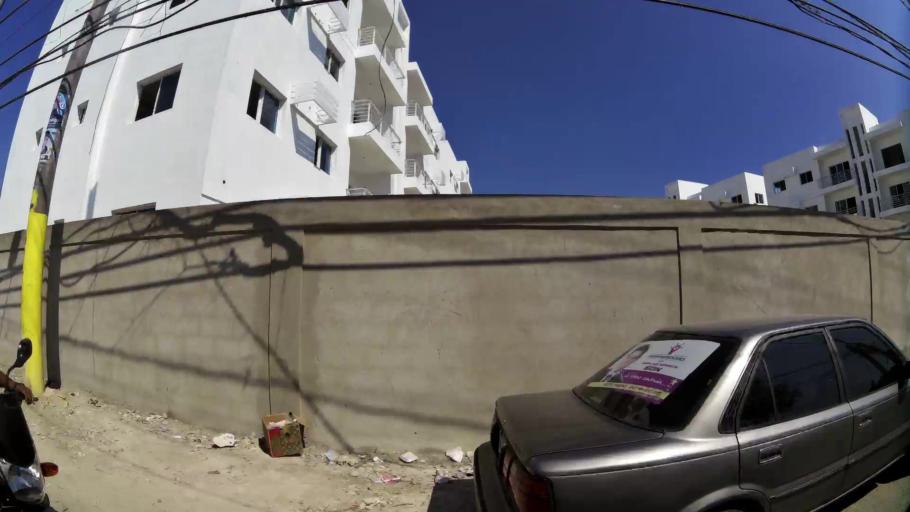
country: DO
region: Santo Domingo
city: Santo Domingo Oeste
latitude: 18.4795
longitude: -70.0012
